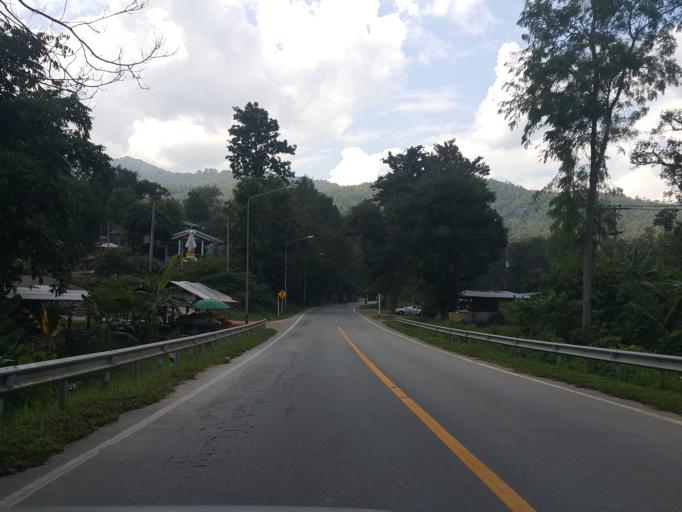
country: TH
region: Chiang Mai
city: Chom Thong
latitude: 18.5291
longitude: 98.6110
